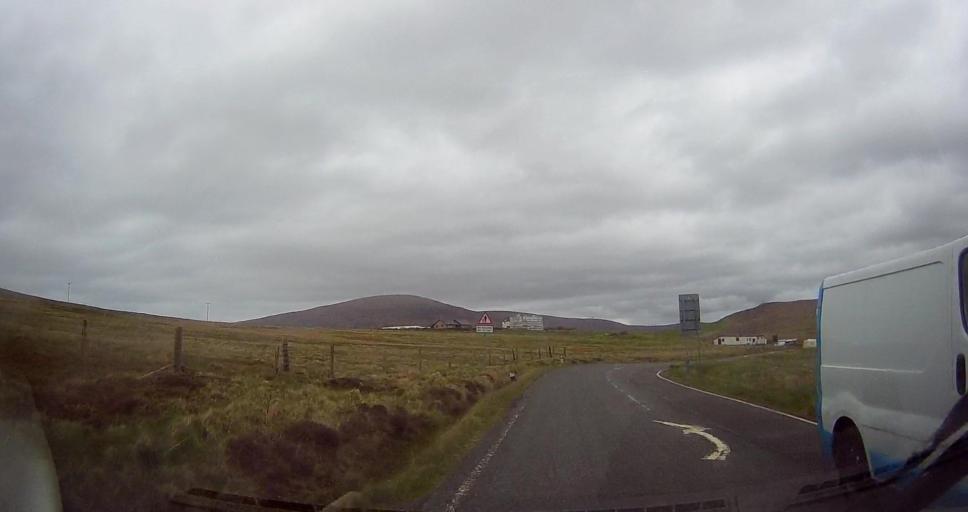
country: GB
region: Scotland
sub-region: Shetland Islands
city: Lerwick
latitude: 60.4887
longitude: -1.4662
